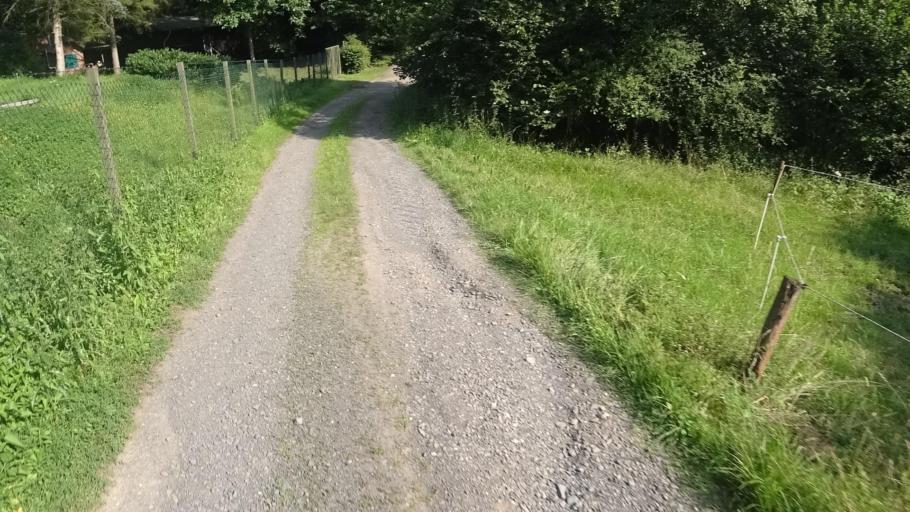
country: DE
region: Rheinland-Pfalz
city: Sankt Katharinen
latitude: 50.5583
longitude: 7.3659
